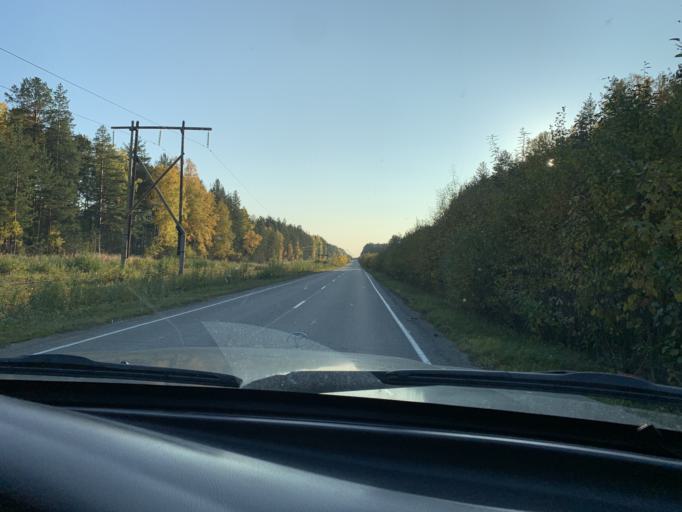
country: RU
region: Sverdlovsk
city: Verkhneye Dubrovo
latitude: 56.8761
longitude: 61.1130
